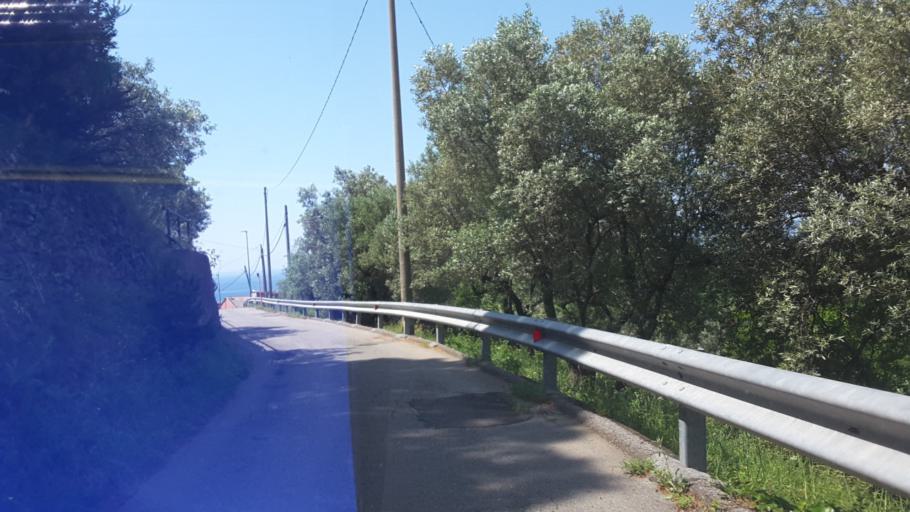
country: IT
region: Liguria
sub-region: Provincia di Genova
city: Mele
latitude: 44.4353
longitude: 8.7889
